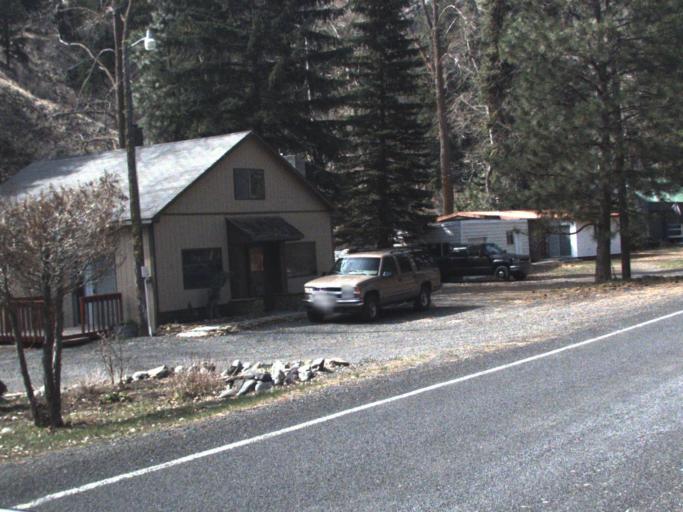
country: US
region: Washington
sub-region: Yakima County
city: Tieton
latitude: 46.8891
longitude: -120.9923
